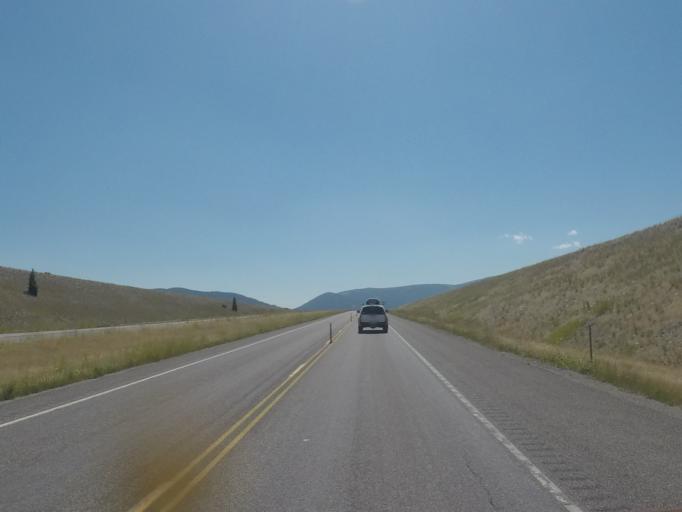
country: US
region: Montana
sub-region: Park County
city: Livingston
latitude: 45.6740
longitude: -110.5172
